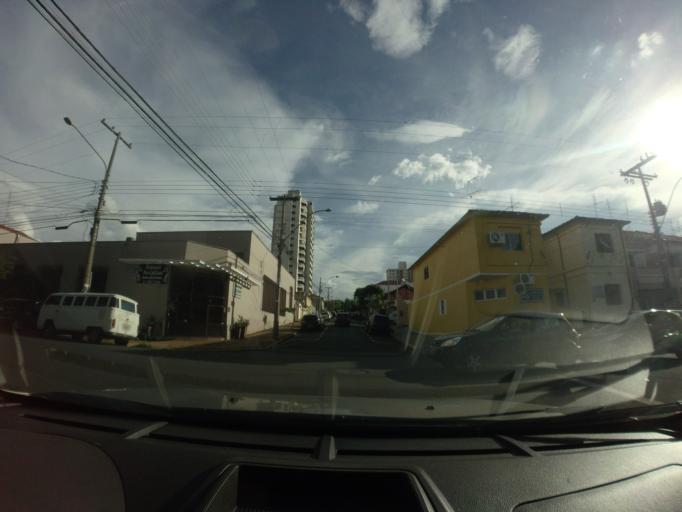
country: BR
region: Sao Paulo
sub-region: Piracicaba
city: Piracicaba
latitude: -22.7269
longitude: -47.6411
